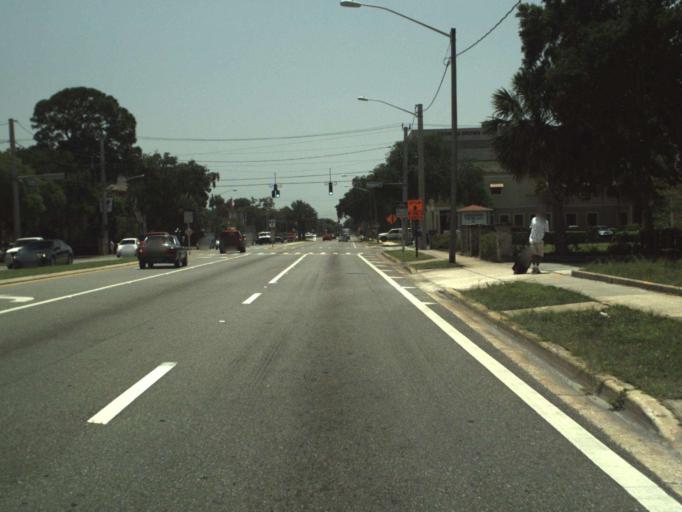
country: US
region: Florida
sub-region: Volusia County
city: Daytona Beach
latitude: 29.2096
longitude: -81.0223
